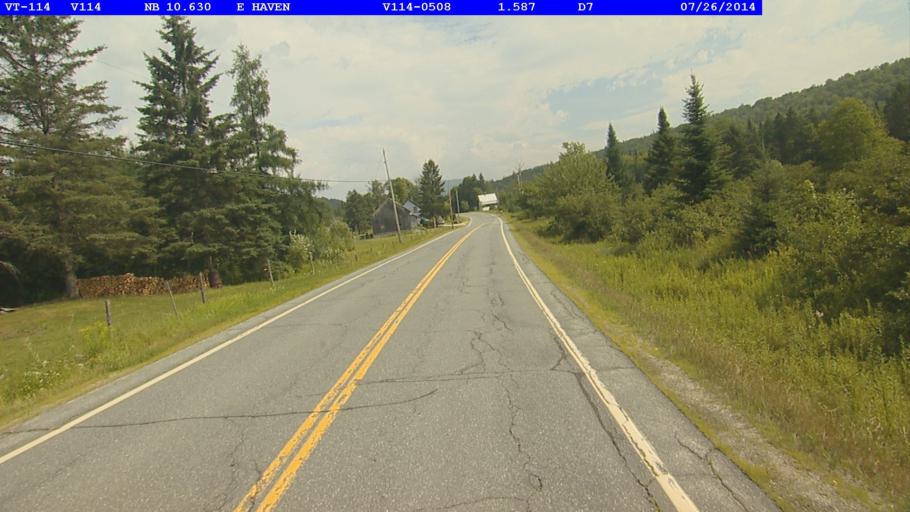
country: US
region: Vermont
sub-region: Caledonia County
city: Lyndonville
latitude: 44.6616
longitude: -71.8904
